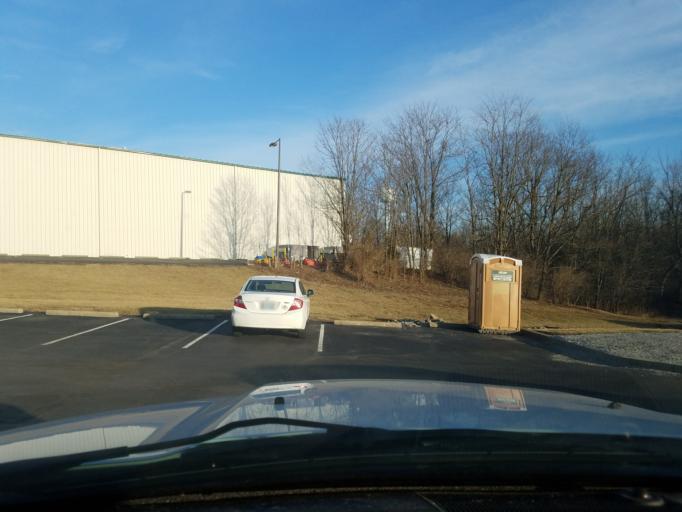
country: US
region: Kentucky
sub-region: Oldham County
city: Buckner
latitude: 38.3729
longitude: -85.4492
